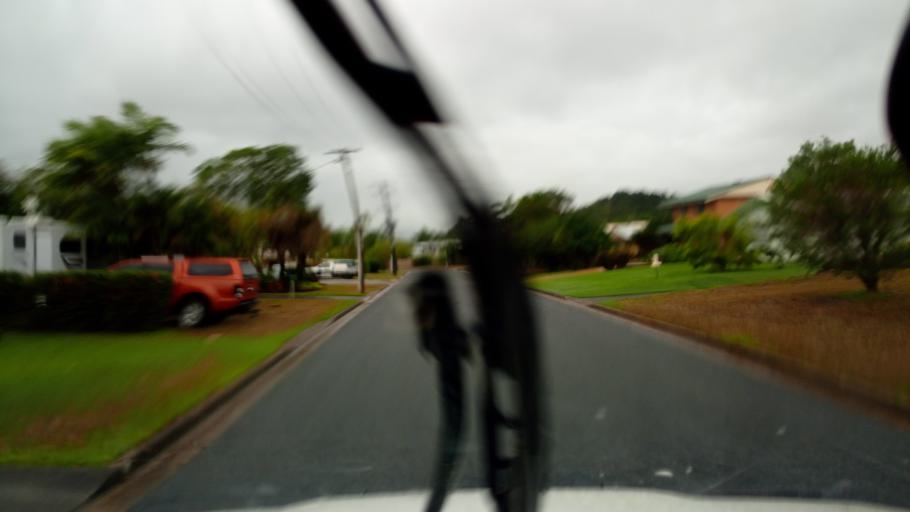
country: AU
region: Queensland
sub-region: Cairns
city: Woree
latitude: -16.9603
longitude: 145.7287
